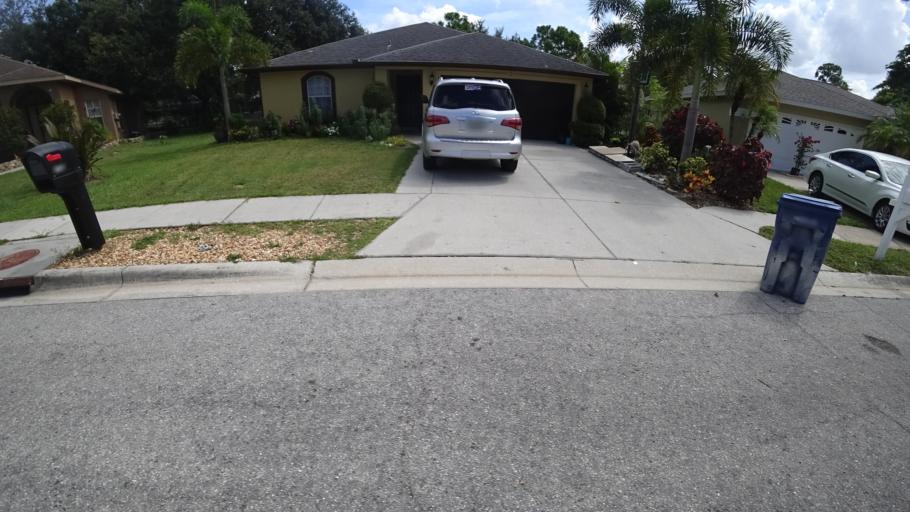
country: US
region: Florida
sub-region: Manatee County
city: Samoset
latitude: 27.4531
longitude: -82.5374
